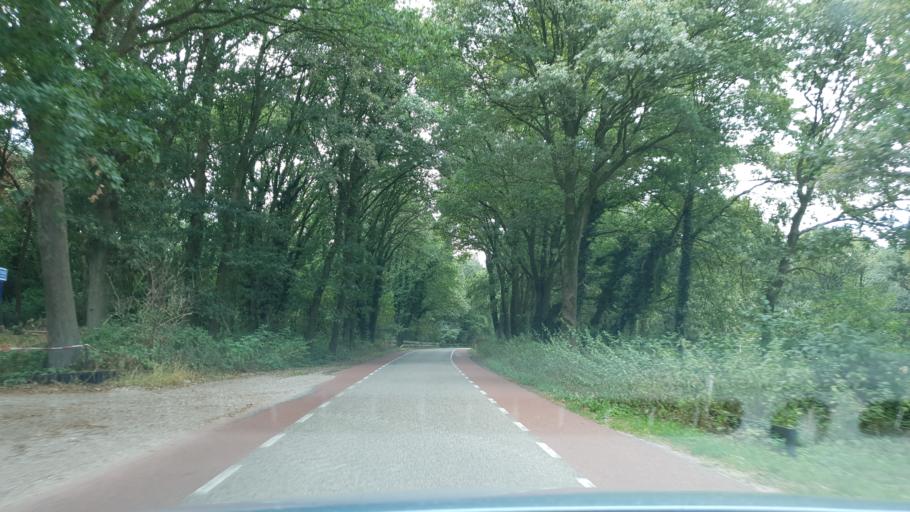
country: NL
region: Gelderland
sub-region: Gemeente Nijmegen
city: Lindenholt
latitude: 51.7766
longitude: 5.8153
